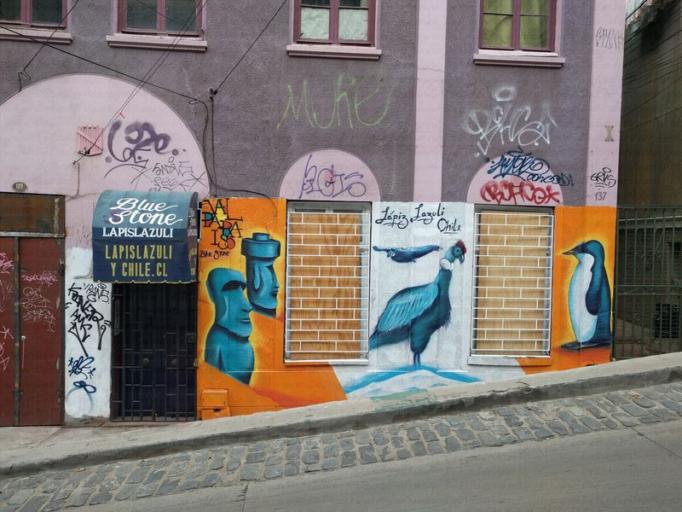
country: CL
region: Valparaiso
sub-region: Provincia de Valparaiso
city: Valparaiso
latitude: -33.0433
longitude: -71.6264
